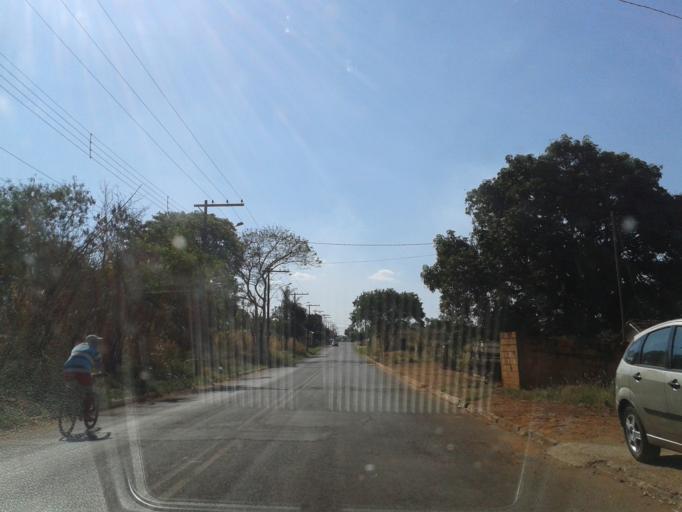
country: BR
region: Minas Gerais
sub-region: Araguari
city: Araguari
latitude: -18.6591
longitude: -48.1785
